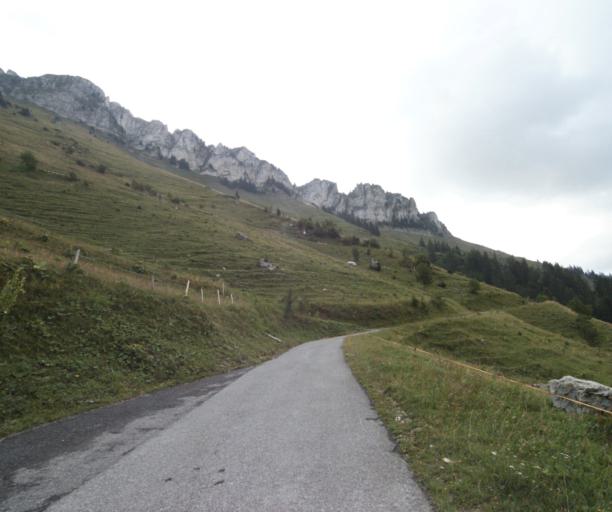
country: CH
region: Vaud
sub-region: Riviera-Pays-d'Enhaut District
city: Caux
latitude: 46.4210
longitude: 6.9949
